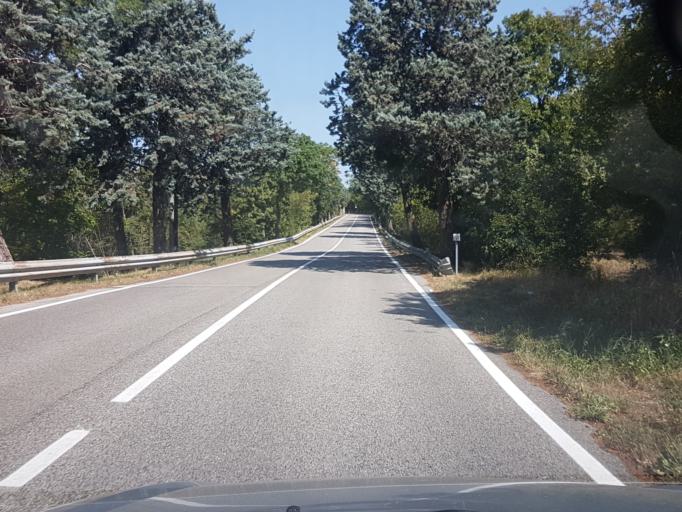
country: IT
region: Friuli Venezia Giulia
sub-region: Provincia di Trieste
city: Aurisina
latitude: 45.7556
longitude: 13.6892
